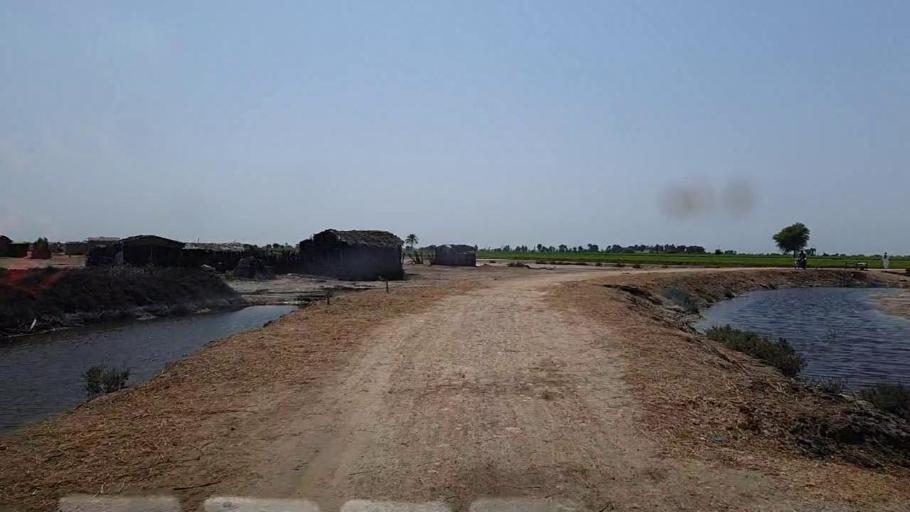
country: PK
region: Sindh
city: Kario
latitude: 24.6348
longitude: 68.4891
